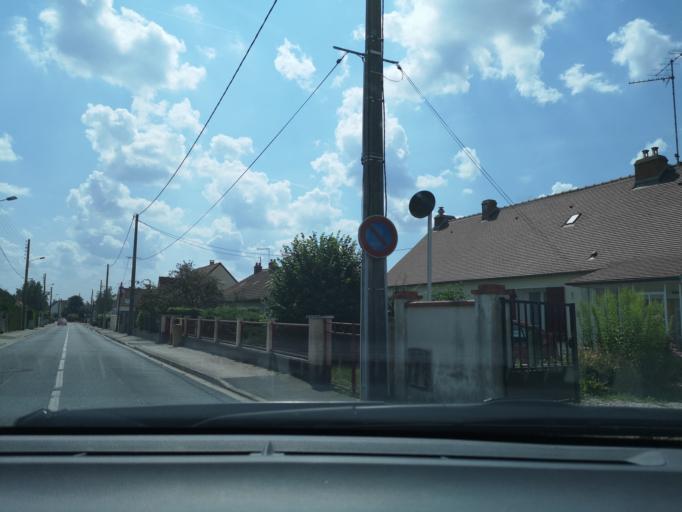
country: FR
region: Centre
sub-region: Departement du Loiret
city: Semoy
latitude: 47.9326
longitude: 1.9400
